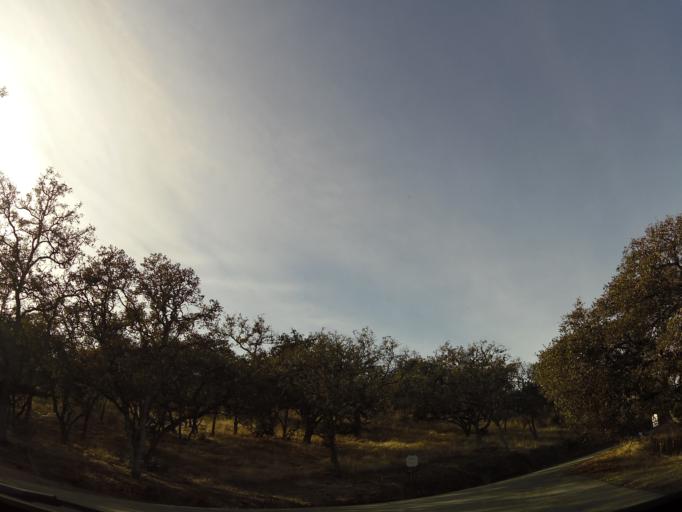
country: US
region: California
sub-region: San Benito County
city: Ridgemark
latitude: 36.7366
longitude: -121.3697
